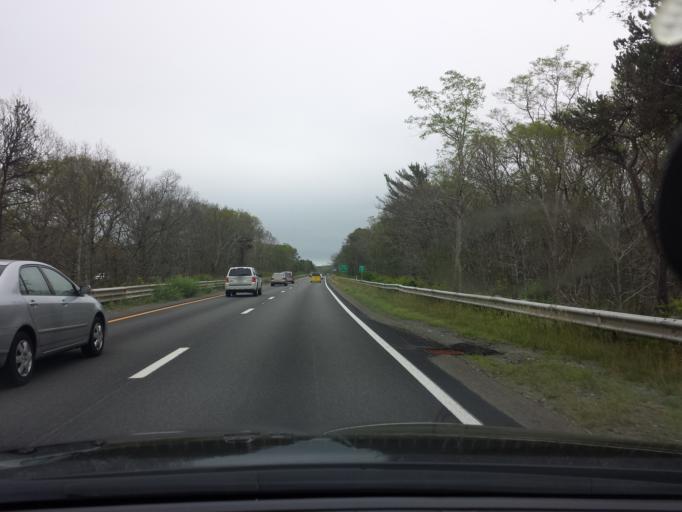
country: US
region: Massachusetts
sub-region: Barnstable County
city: West Barnstable
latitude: 41.7141
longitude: -70.4164
